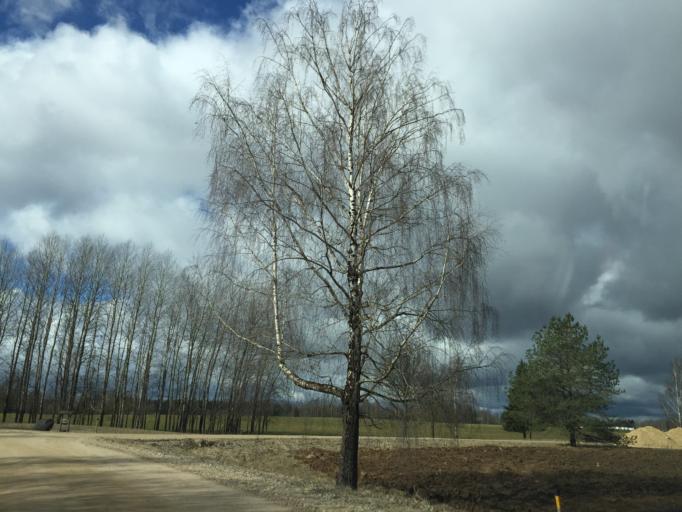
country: LV
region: Akniste
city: Akniste
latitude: 56.1071
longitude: 25.9463
